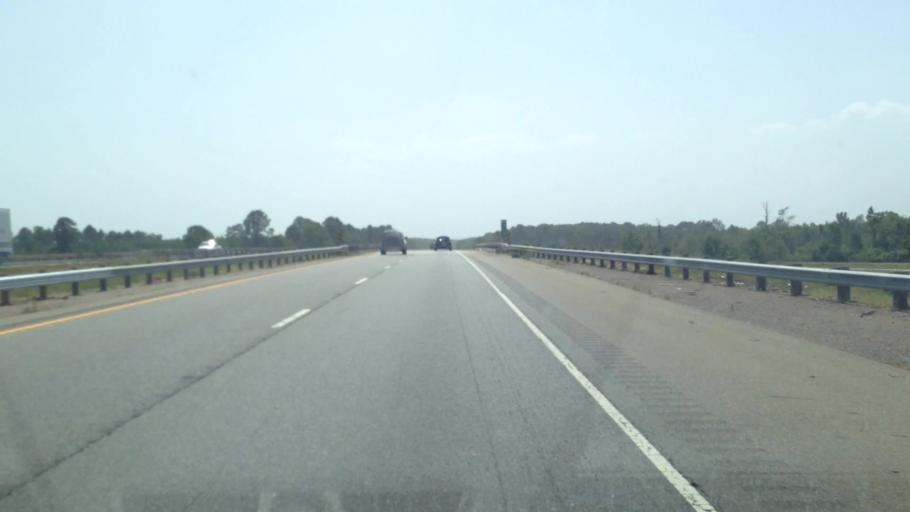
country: US
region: Louisiana
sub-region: Bossier Parish
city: Haughton
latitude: 32.5792
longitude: -93.4309
